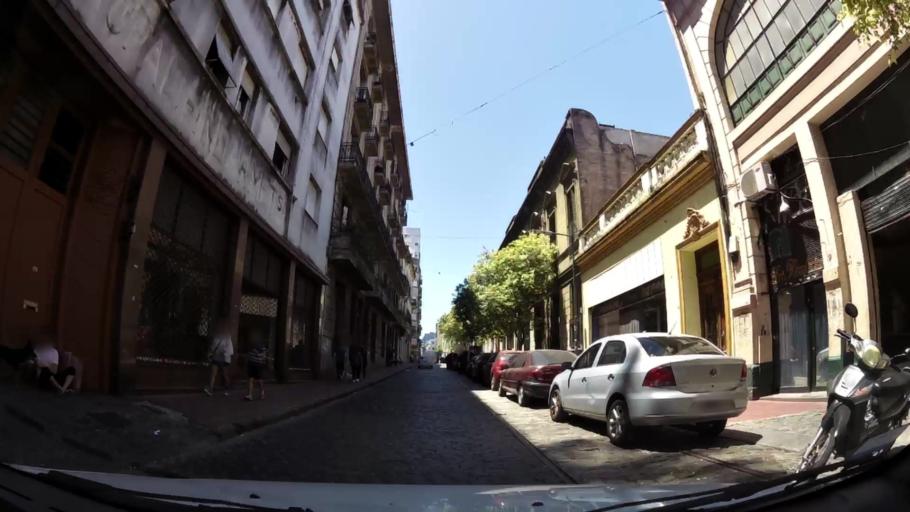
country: AR
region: Buenos Aires F.D.
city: Buenos Aires
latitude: -34.6184
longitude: -58.3726
